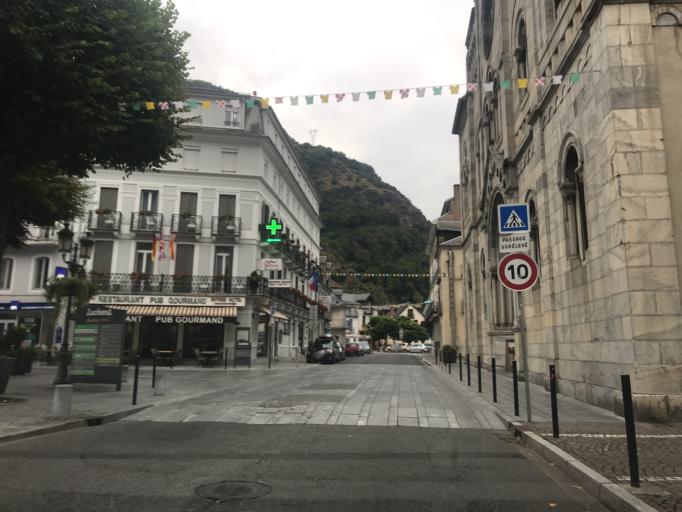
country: FR
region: Midi-Pyrenees
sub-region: Departement de la Haute-Garonne
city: Bagneres-de-Luchon
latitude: 42.7910
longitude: 0.5912
